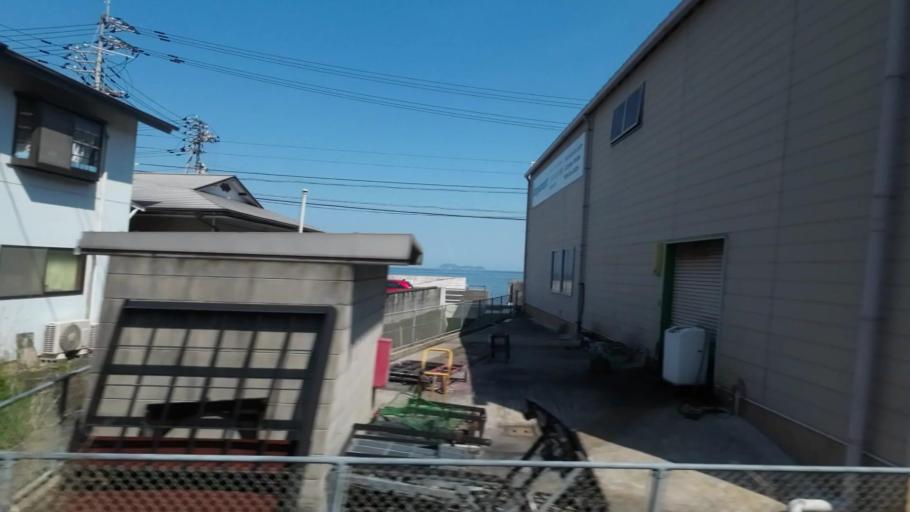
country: JP
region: Ehime
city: Kawanoecho
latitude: 34.0334
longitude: 133.5914
